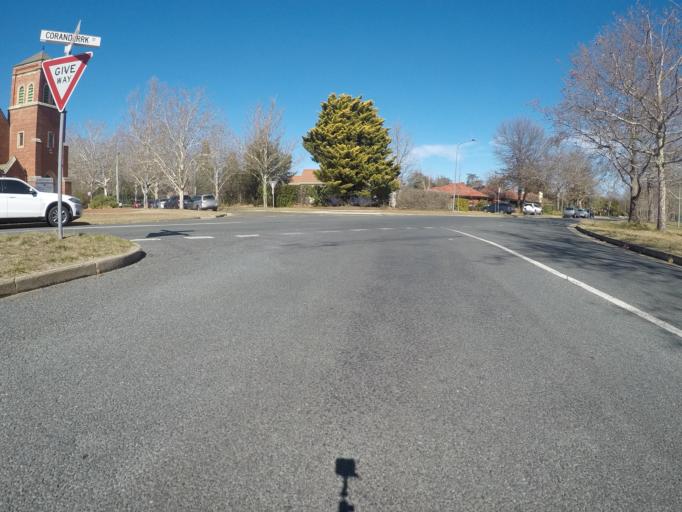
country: AU
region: Australian Capital Territory
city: Canberra
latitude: -35.2802
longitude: 149.1398
